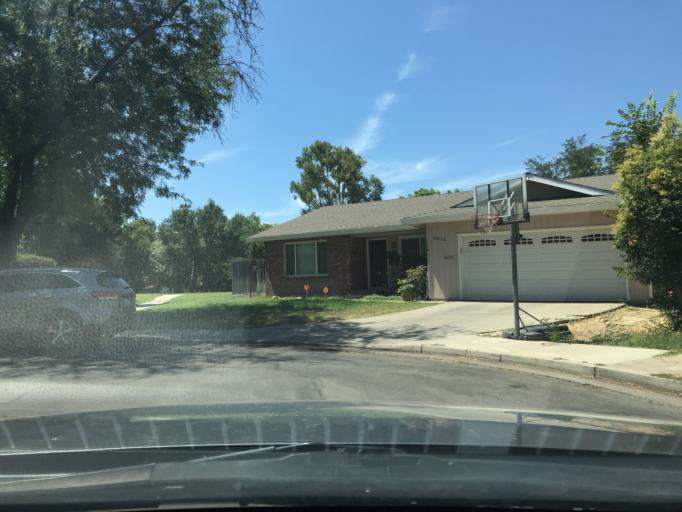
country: US
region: California
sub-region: Merced County
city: Merced
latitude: 37.3255
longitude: -120.4816
